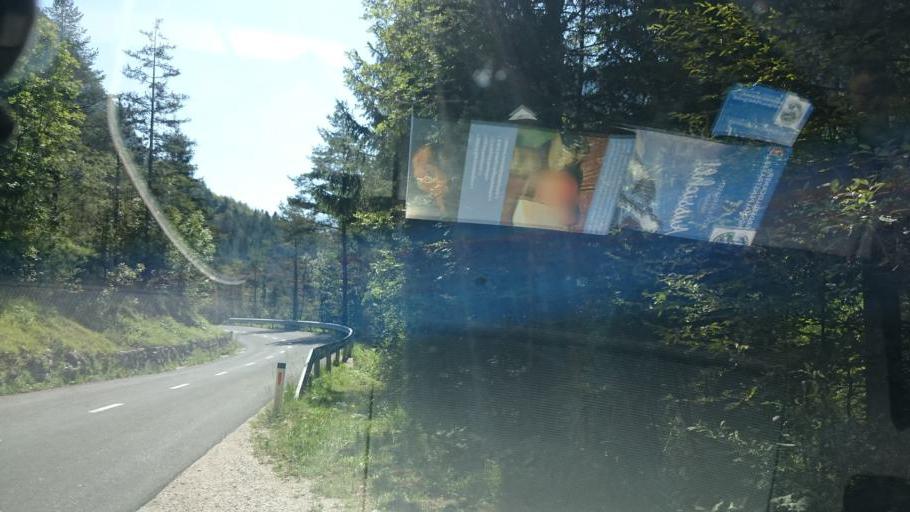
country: SI
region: Bovec
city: Bovec
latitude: 46.3804
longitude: 13.5849
